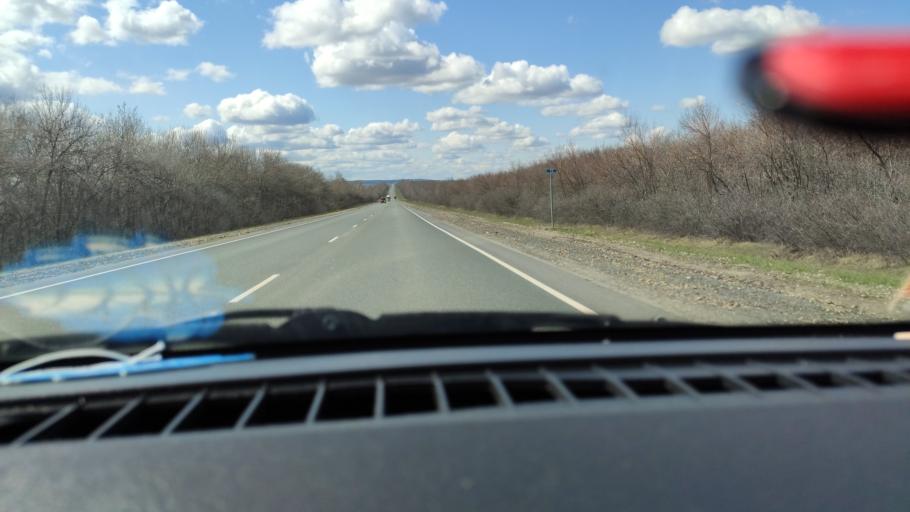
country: RU
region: Saratov
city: Khvalynsk
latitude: 52.6101
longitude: 48.1576
